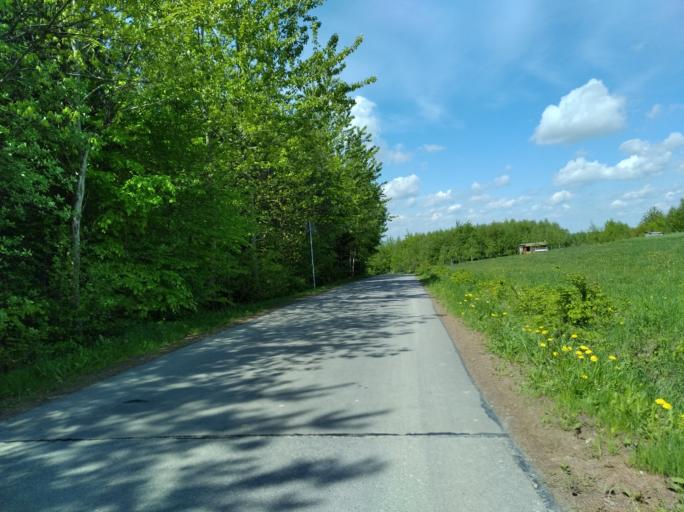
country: PL
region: Subcarpathian Voivodeship
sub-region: Powiat jasielski
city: Kolaczyce
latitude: 49.8370
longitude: 21.5079
